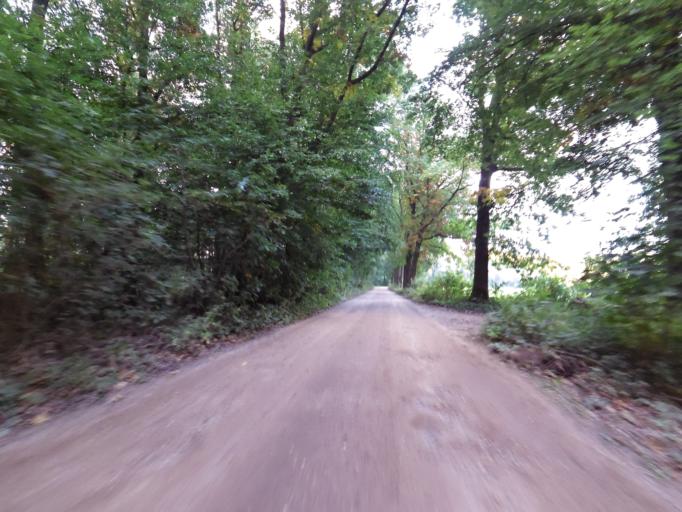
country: NL
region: Gelderland
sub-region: Gemeente Doesburg
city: Doesburg
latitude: 51.9473
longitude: 6.1950
